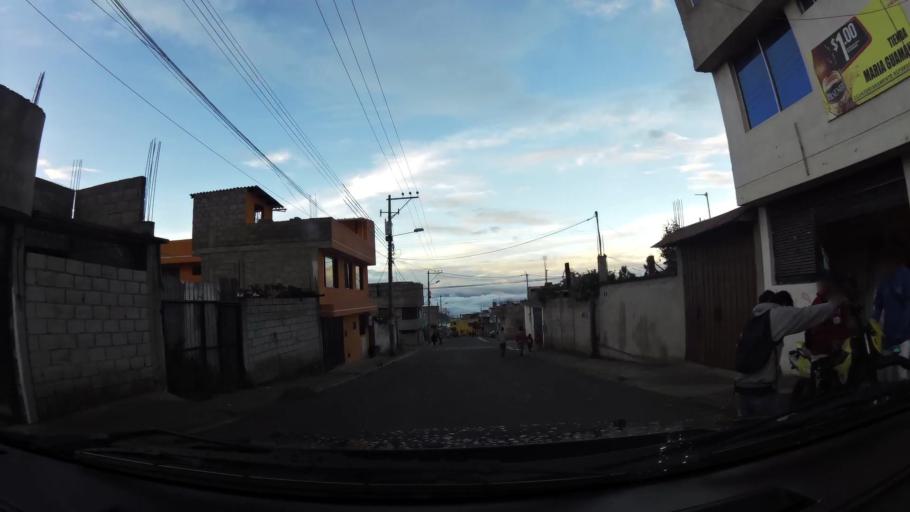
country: EC
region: Pichincha
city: Quito
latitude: -0.1003
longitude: -78.5216
